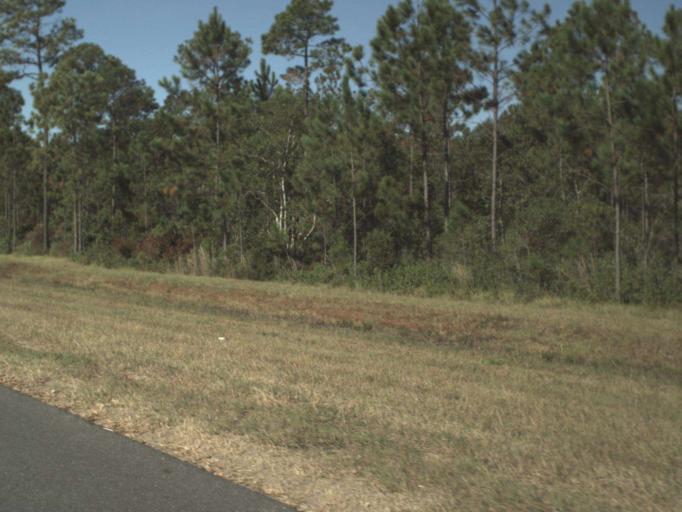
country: US
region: Florida
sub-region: Walton County
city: Freeport
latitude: 30.4425
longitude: -86.1433
